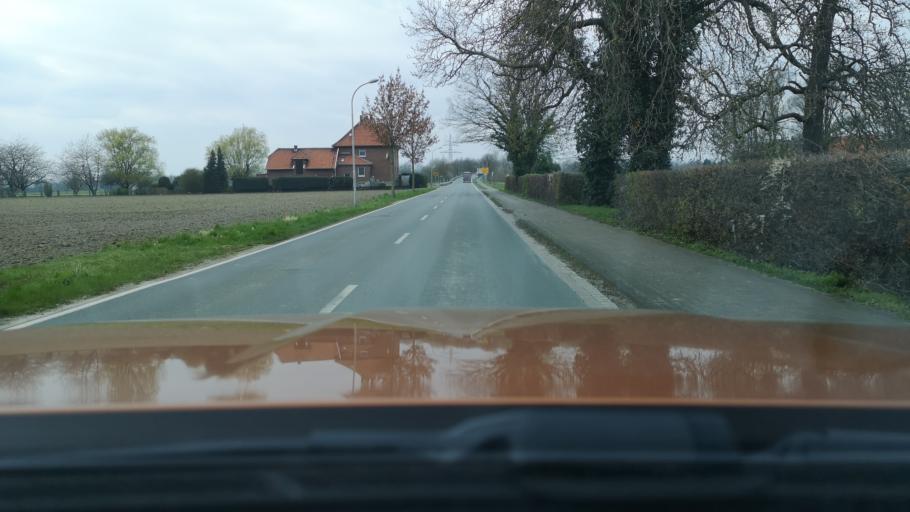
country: DE
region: Lower Saxony
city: Seggebruch
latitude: 52.2913
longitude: 9.0965
